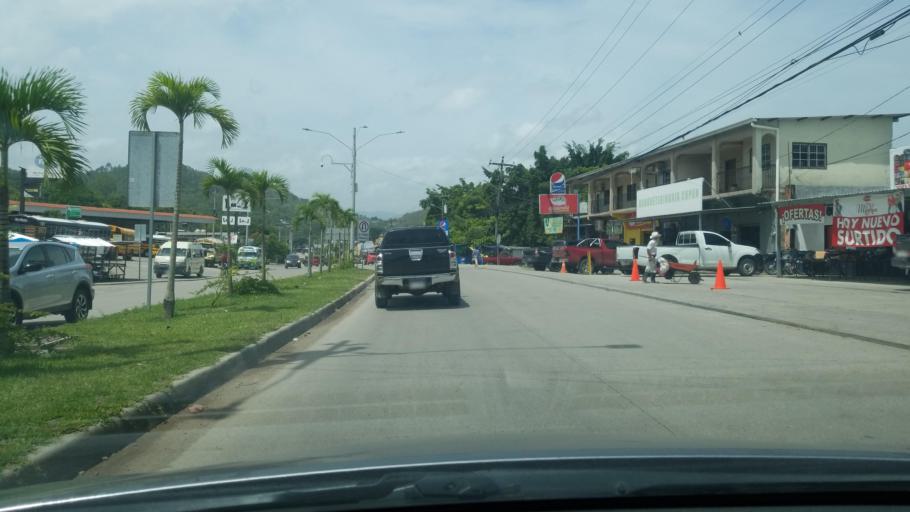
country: HN
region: Copan
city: La Entrada
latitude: 15.0580
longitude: -88.7545
